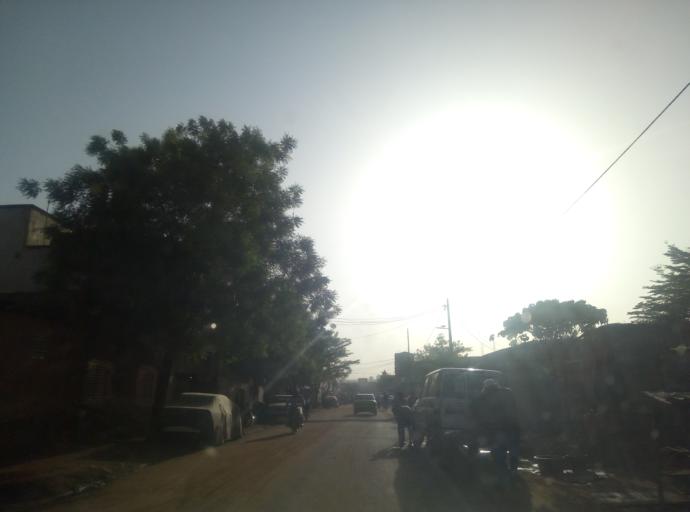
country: ML
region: Bamako
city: Bamako
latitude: 12.6031
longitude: -7.9651
